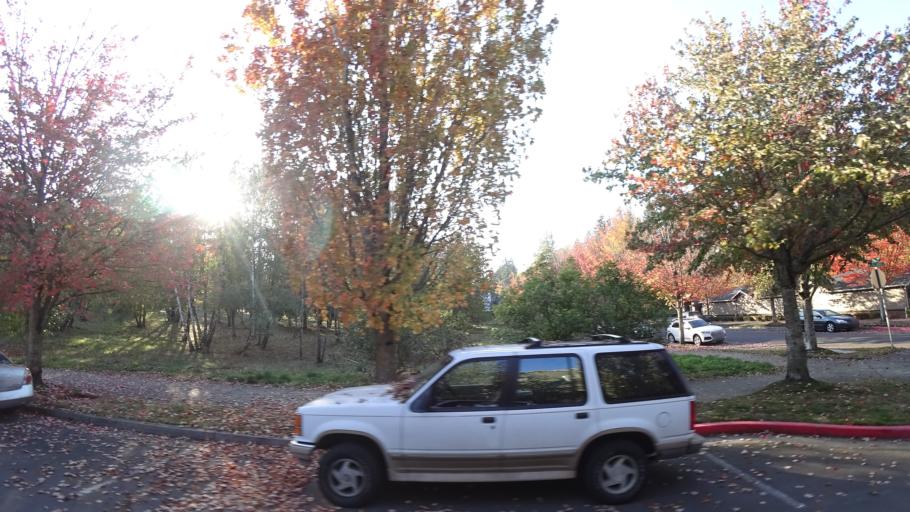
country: US
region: Oregon
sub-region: Multnomah County
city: Gresham
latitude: 45.5065
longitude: -122.4436
